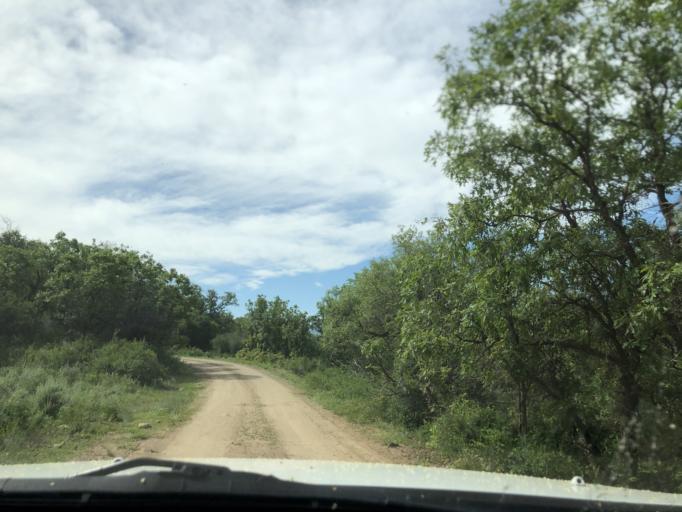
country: US
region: Colorado
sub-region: Delta County
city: Paonia
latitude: 39.0080
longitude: -107.3418
